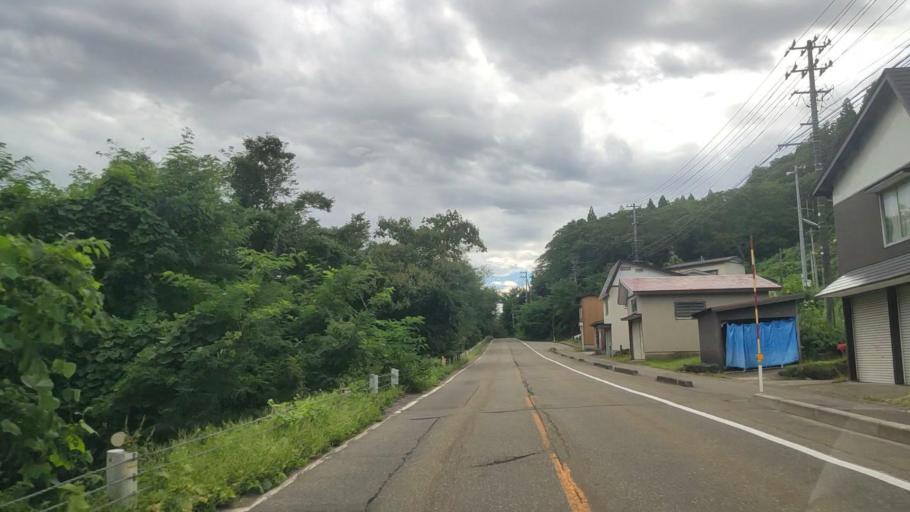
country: JP
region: Niigata
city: Arai
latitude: 36.9983
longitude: 138.2669
